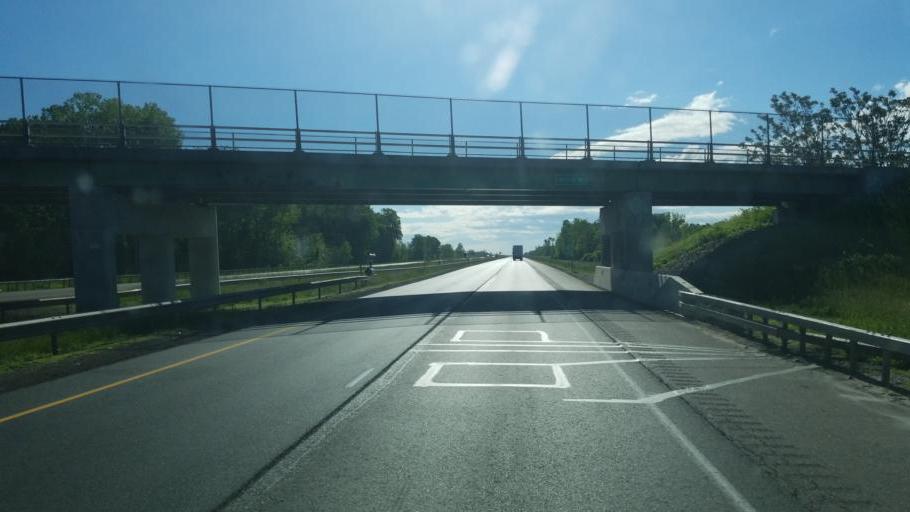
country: US
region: New York
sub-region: Livingston County
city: Caledonia
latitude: 43.0300
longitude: -77.8953
